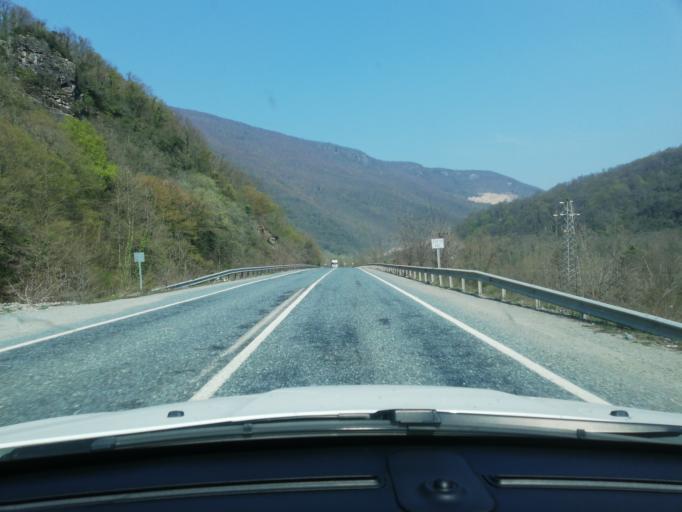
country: TR
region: Zonguldak
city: Gokcebey
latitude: 41.2592
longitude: 32.1555
